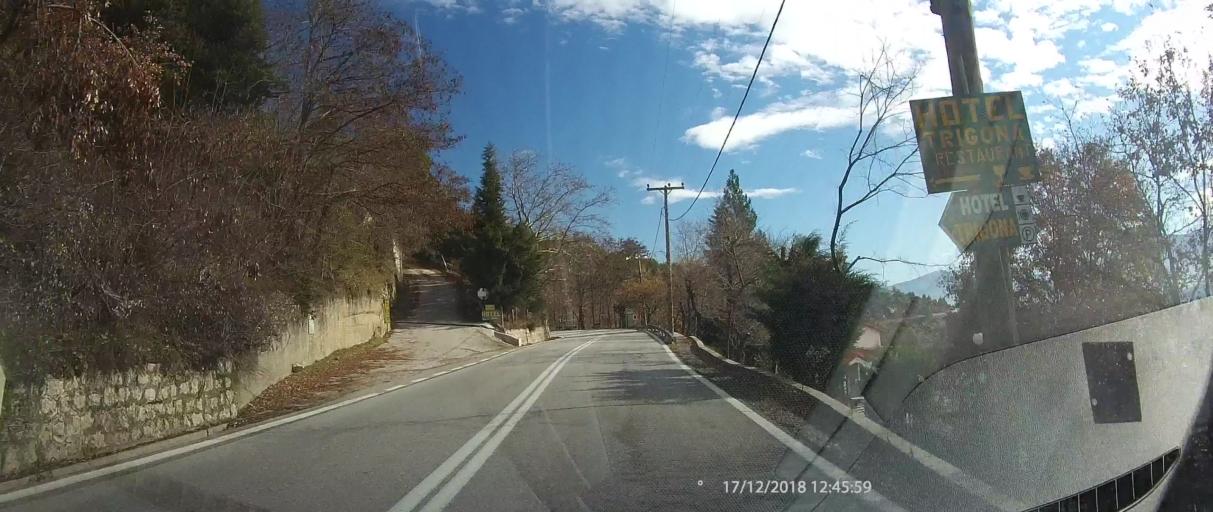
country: GR
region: Thessaly
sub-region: Trikala
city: Kastraki
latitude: 39.7882
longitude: 21.4138
